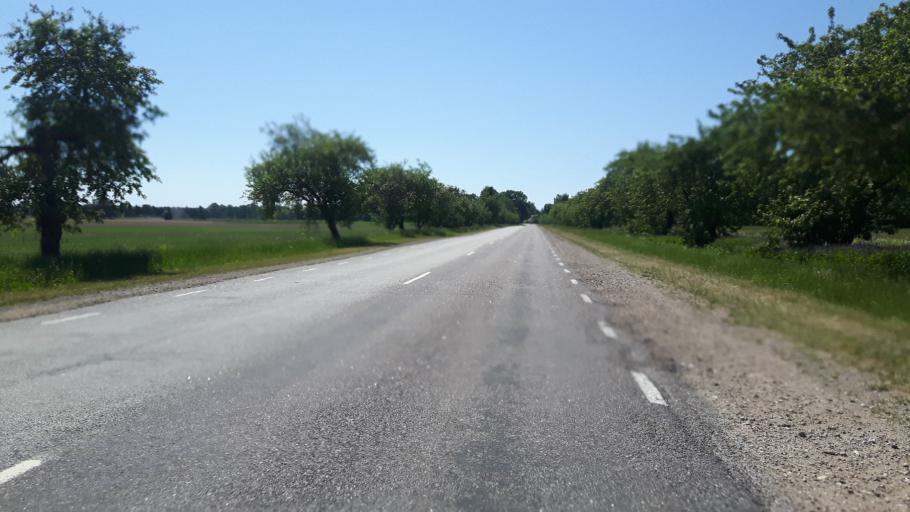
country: EE
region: Paernumaa
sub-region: Tootsi vald
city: Tootsi
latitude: 58.4722
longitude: 24.7972
